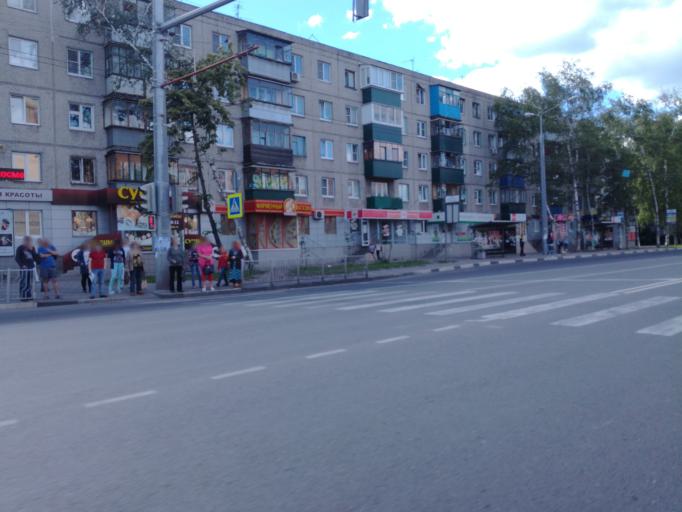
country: RU
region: Kursk
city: Kursk
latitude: 51.7585
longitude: 36.1873
